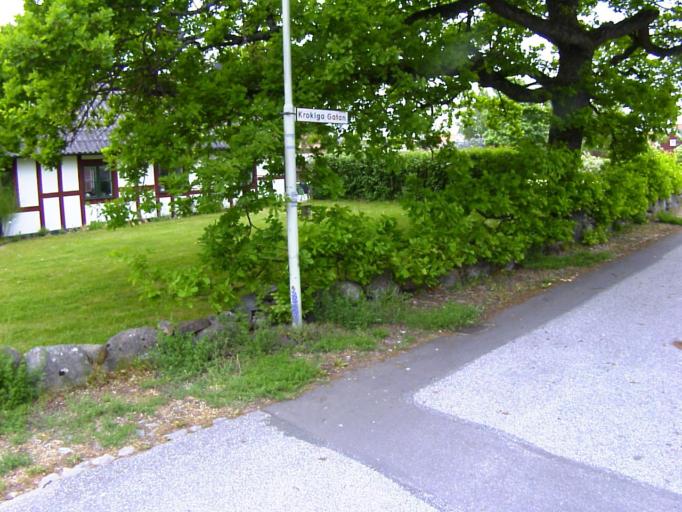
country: SE
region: Skane
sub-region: Kristianstads Kommun
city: Ahus
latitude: 55.9216
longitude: 14.2880
